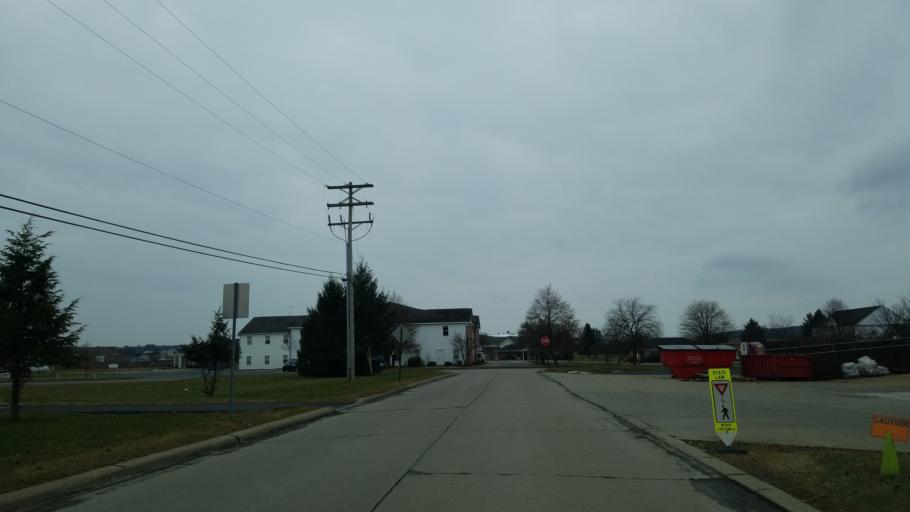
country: US
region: Pennsylvania
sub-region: Clearfield County
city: DuBois
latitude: 41.1210
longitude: -78.7482
